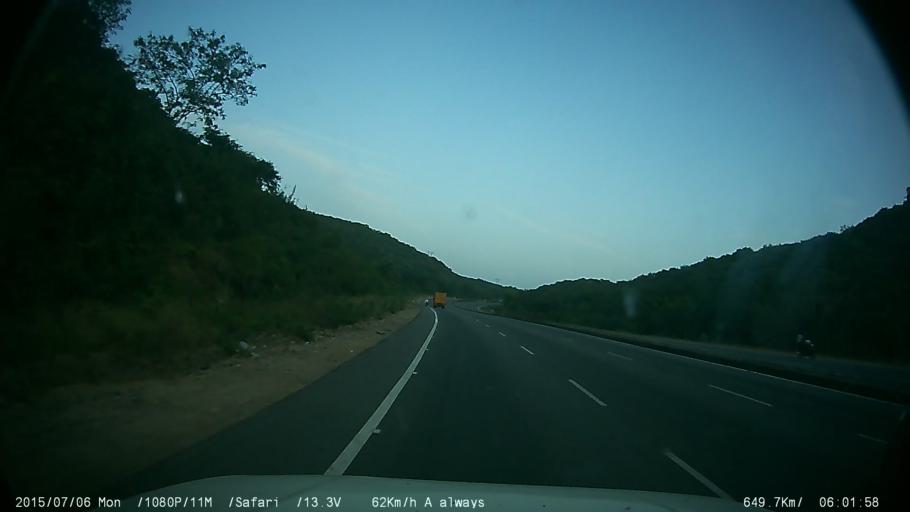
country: IN
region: Tamil Nadu
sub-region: Krishnagiri
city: Krishnagiri
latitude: 12.6062
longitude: 78.1126
